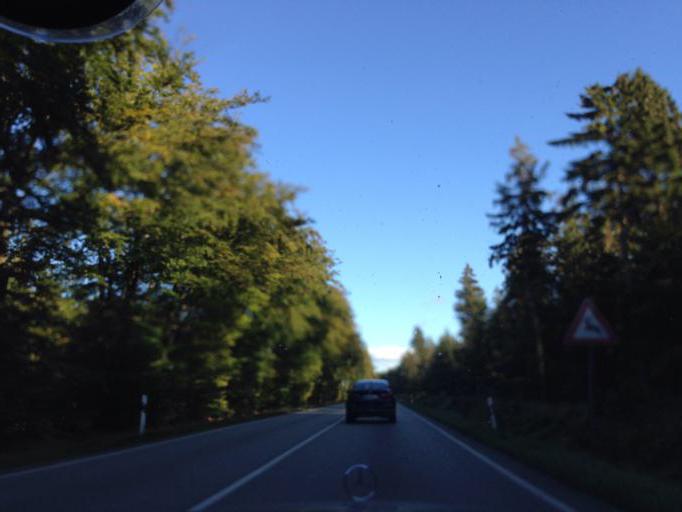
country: DE
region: Schleswig-Holstein
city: Rickling
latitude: 54.0197
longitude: 10.1345
